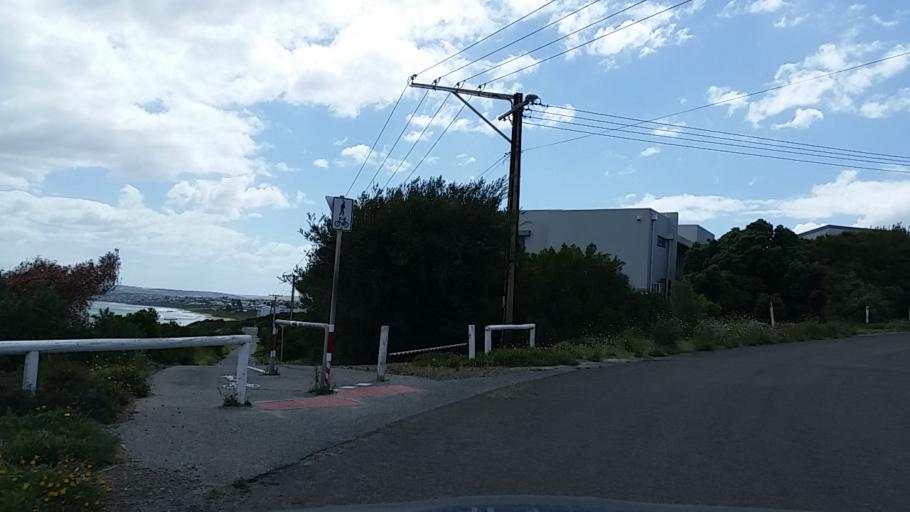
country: AU
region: South Australia
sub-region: Alexandrina
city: Port Elliot
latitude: -35.5352
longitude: 138.6765
